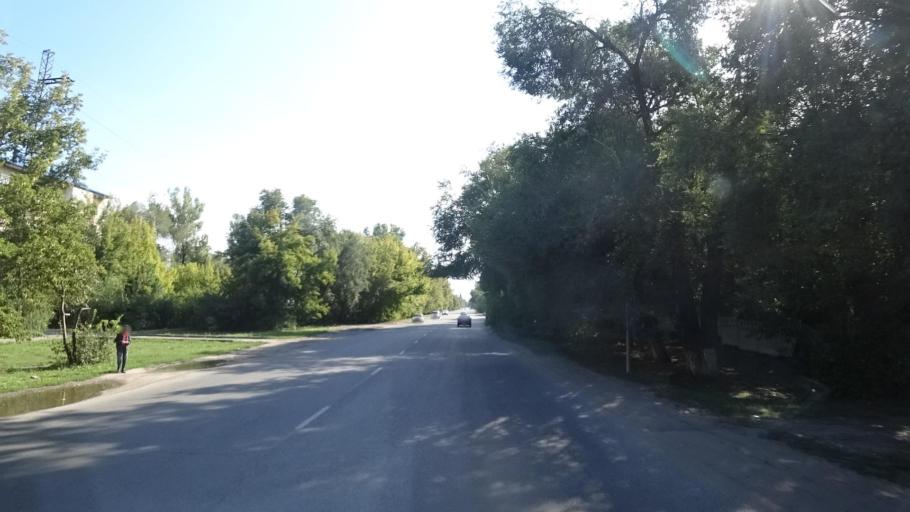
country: KZ
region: Almaty Oblysy
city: Energeticheskiy
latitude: 43.3907
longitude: 77.0034
